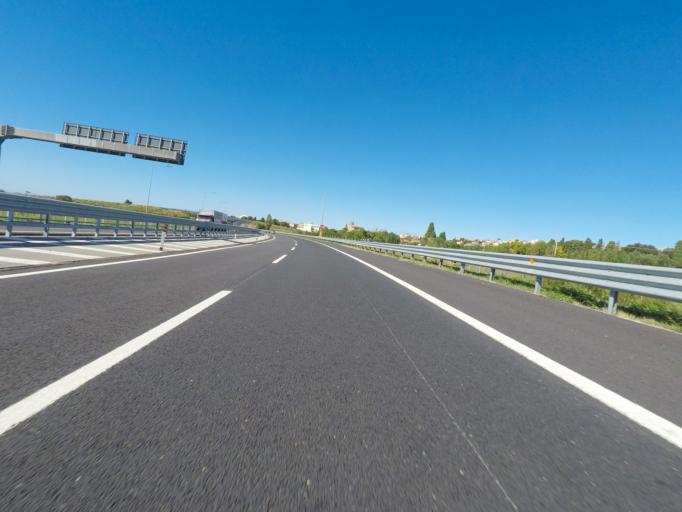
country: IT
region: Latium
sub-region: Provincia di Viterbo
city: Tarquinia
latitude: 42.2388
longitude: 11.7598
